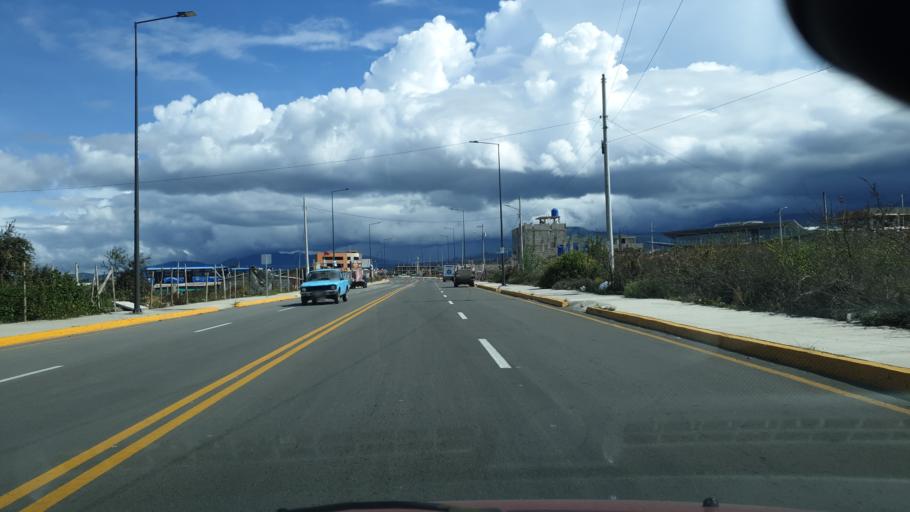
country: EC
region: Tungurahua
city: Ambato
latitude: -1.2969
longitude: -78.6314
